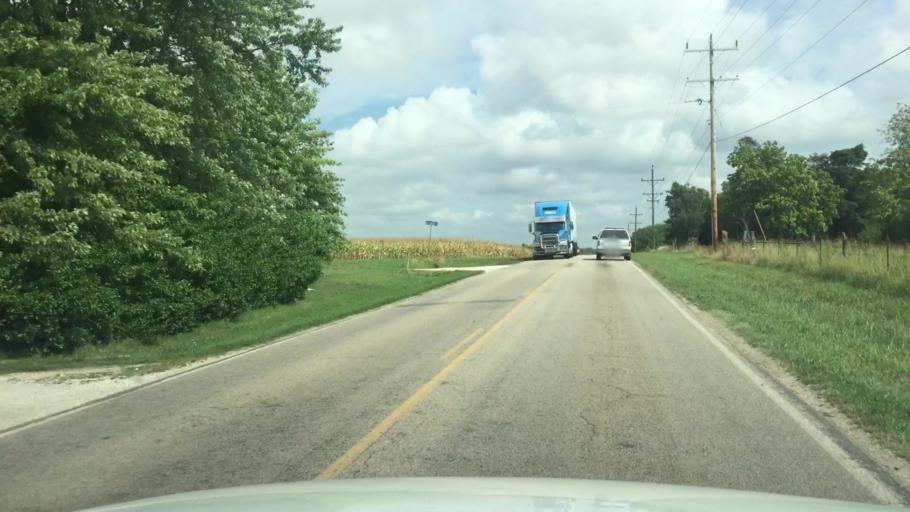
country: US
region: Kansas
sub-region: Allen County
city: Humboldt
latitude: 37.8380
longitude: -95.4368
